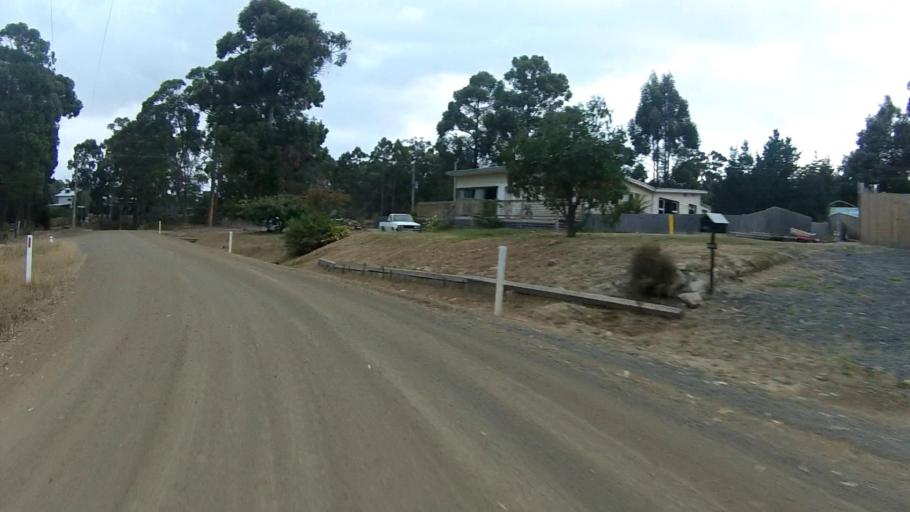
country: AU
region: Tasmania
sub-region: Huon Valley
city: Cygnet
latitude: -43.2288
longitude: 147.0988
